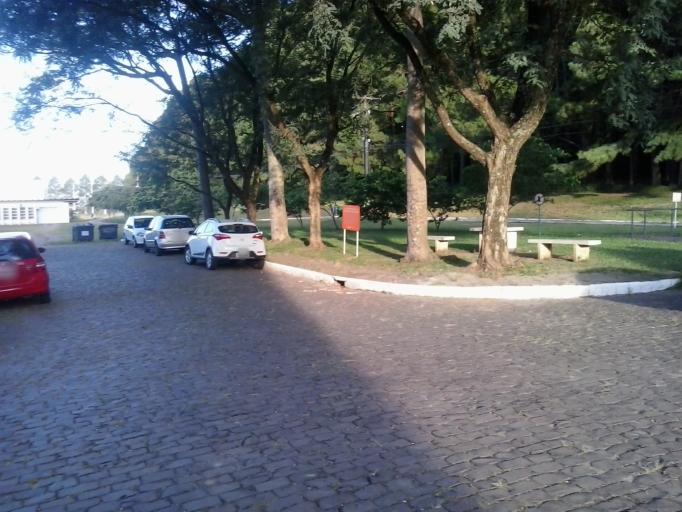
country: BR
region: Rio Grande do Sul
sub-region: Santa Maria
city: Santa Maria
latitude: -29.7212
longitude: -53.7144
